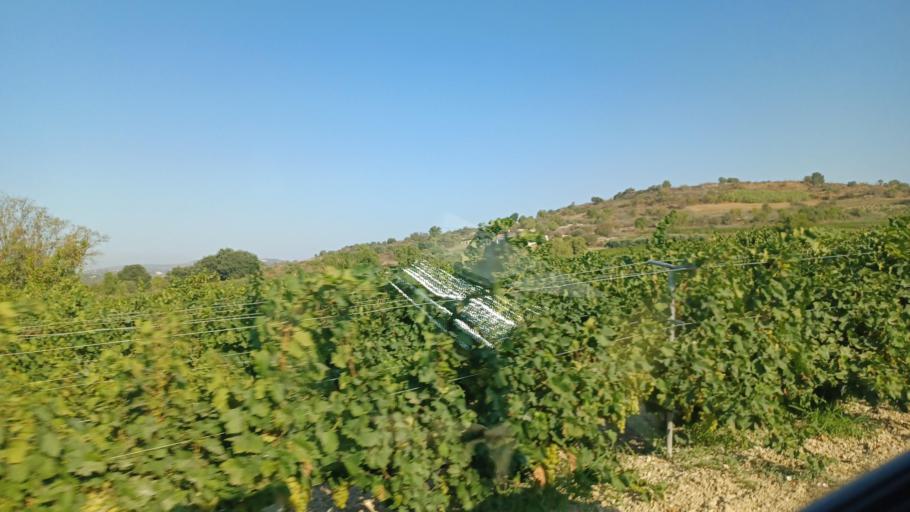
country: CY
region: Pafos
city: Tala
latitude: 34.8922
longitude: 32.5041
